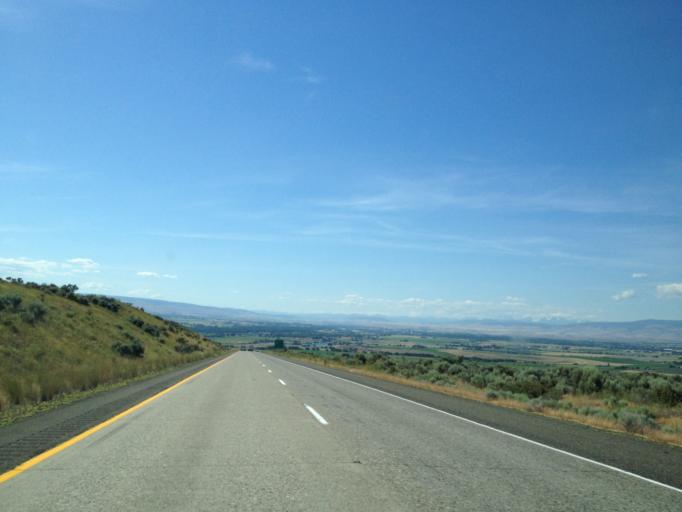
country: US
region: Washington
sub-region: Kittitas County
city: Kittitas
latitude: 46.9064
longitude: -120.4605
